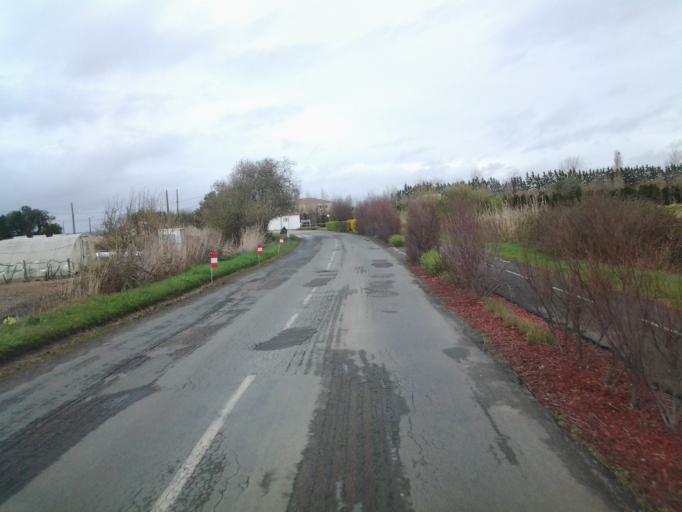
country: FR
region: Pays de la Loire
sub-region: Departement de la Vendee
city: La Tranche-sur-Mer
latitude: 46.3593
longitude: -1.4522
